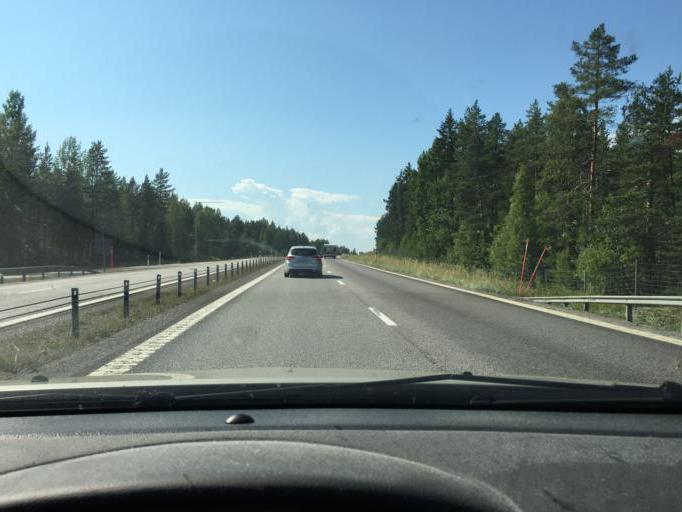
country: SE
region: Norrbotten
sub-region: Lulea Kommun
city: Gammelstad
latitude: 65.5829
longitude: 21.9959
